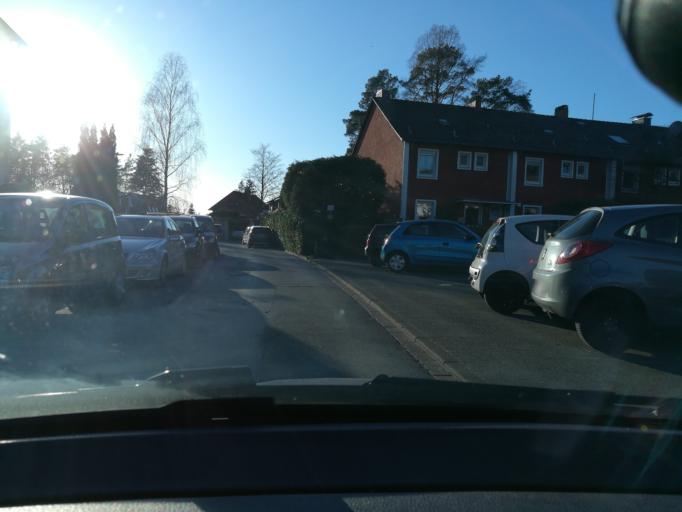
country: DE
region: North Rhine-Westphalia
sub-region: Regierungsbezirk Detmold
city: Oerlinghausen
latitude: 51.9561
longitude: 8.5955
